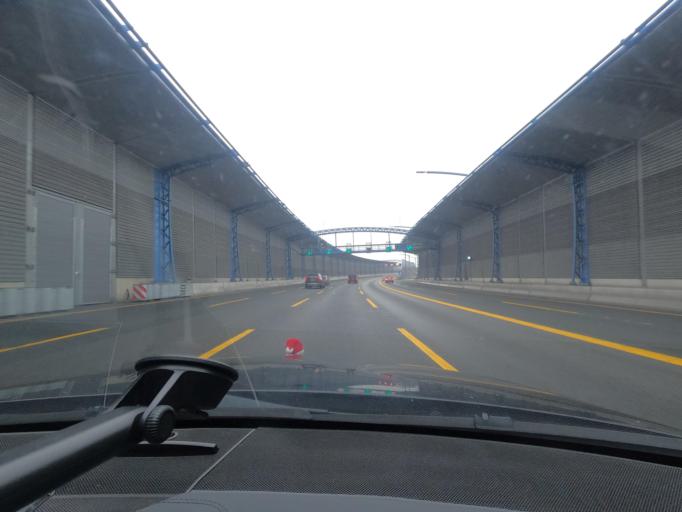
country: DE
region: Hamburg
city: Eidelstedt
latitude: 53.6020
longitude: 9.9179
